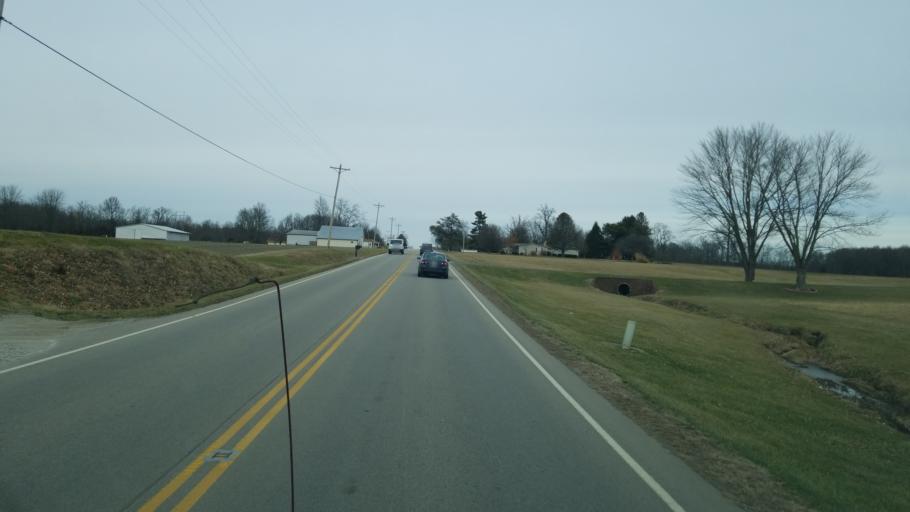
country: US
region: Ohio
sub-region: Adams County
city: Winchester
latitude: 39.0756
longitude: -83.6864
